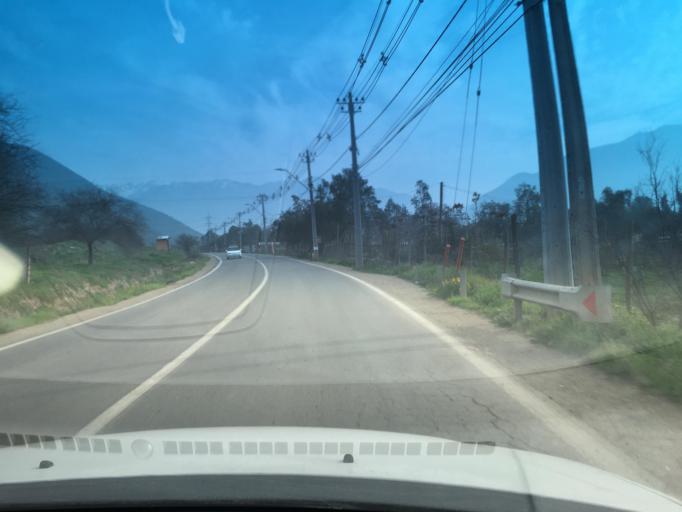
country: CL
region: Santiago Metropolitan
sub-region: Provincia de Chacabuco
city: Lampa
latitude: -33.2724
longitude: -70.8911
